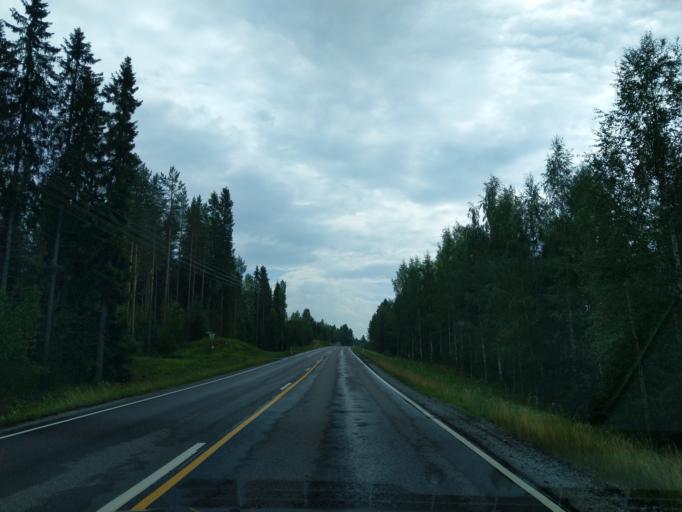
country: FI
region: South Karelia
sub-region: Imatra
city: Parikkala
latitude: 61.6430
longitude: 29.4257
